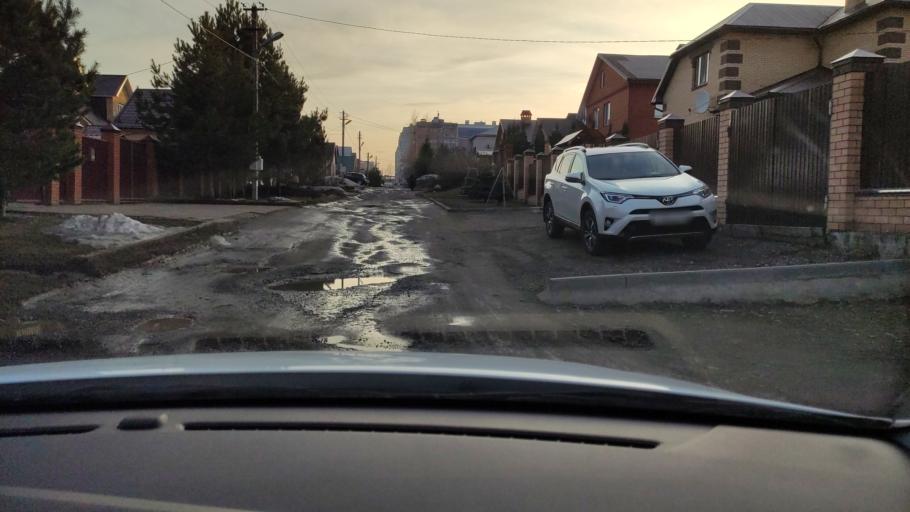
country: RU
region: Tatarstan
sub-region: Gorod Kazan'
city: Kazan
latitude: 55.7868
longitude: 49.2413
